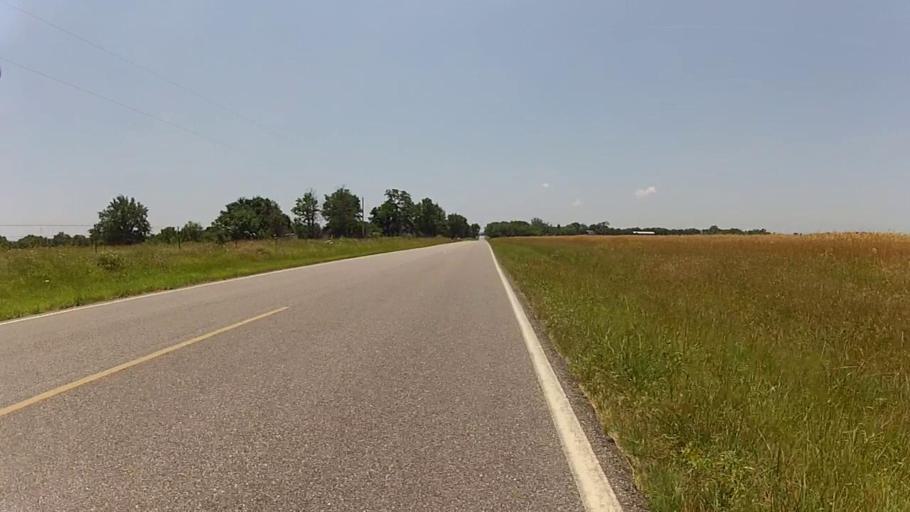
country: US
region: Kansas
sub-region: Montgomery County
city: Cherryvale
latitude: 37.2500
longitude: -95.5371
